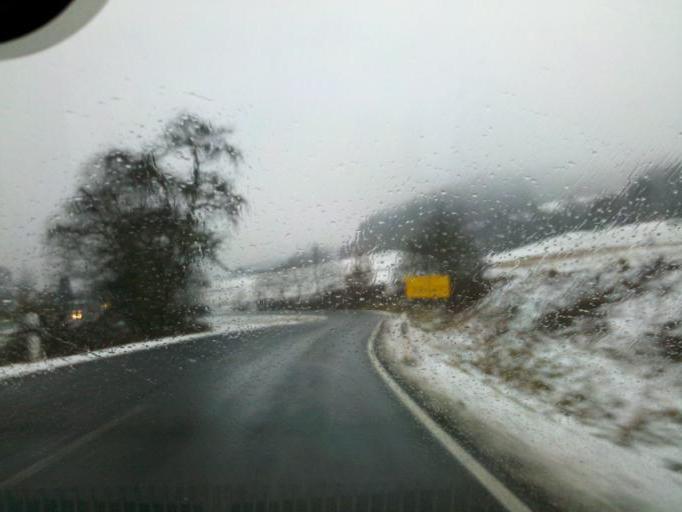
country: DE
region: Hesse
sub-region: Regierungsbezirk Giessen
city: Siegbach
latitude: 50.8274
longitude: 8.3807
